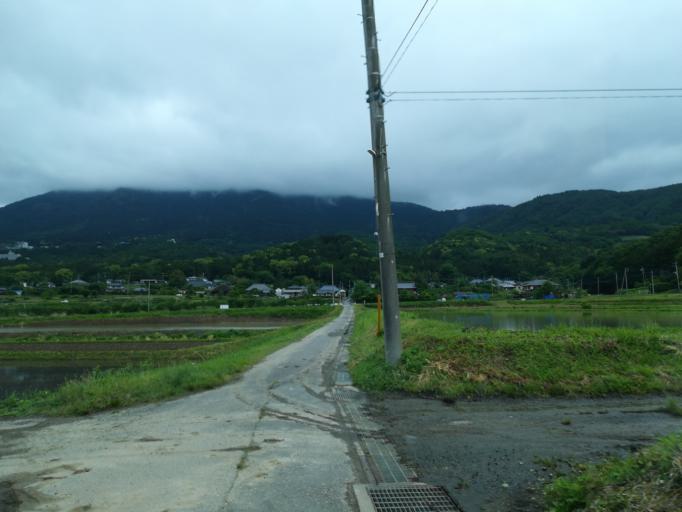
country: JP
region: Ibaraki
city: Tsukuba
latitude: 36.1955
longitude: 140.1103
